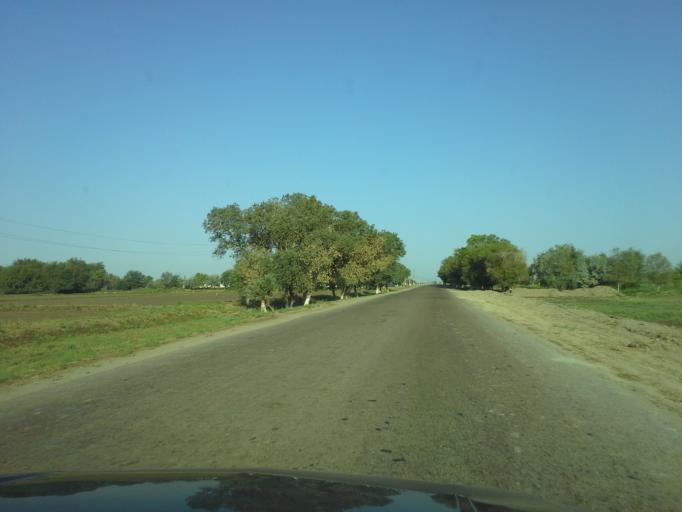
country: UZ
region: Karakalpakstan
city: Khujayli
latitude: 42.2191
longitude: 59.4936
